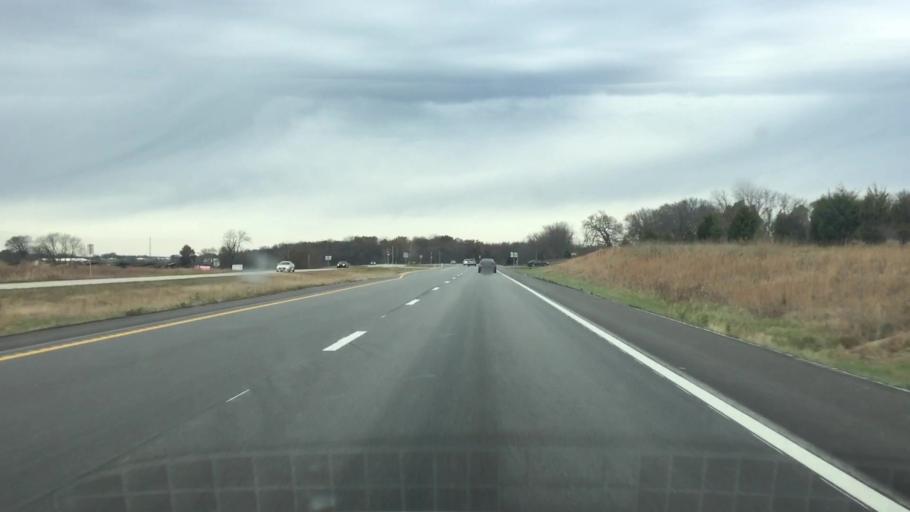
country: US
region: Missouri
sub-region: Saint Clair County
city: Osceola
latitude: 38.0082
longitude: -93.6571
